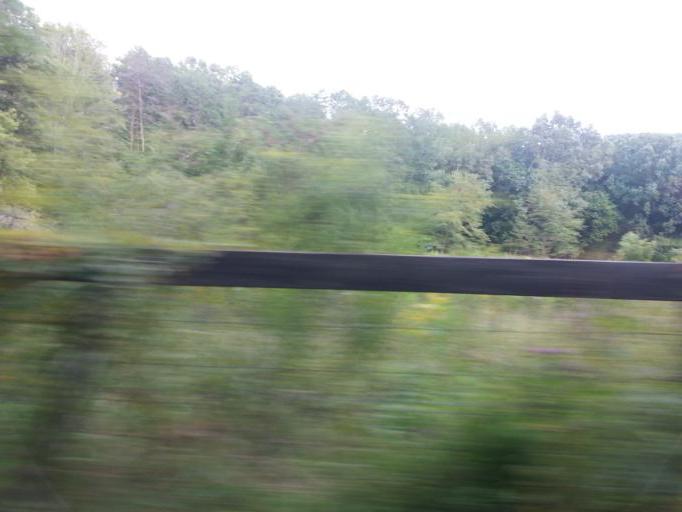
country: US
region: Tennessee
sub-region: Union County
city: Condon
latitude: 36.1203
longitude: -83.7731
